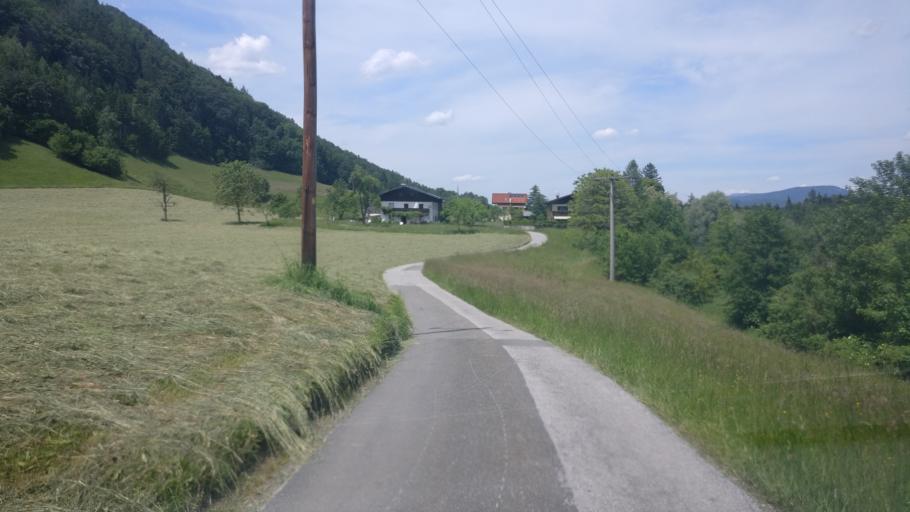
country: AT
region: Salzburg
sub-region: Politischer Bezirk Hallein
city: Adnet
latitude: 47.6517
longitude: 13.1208
